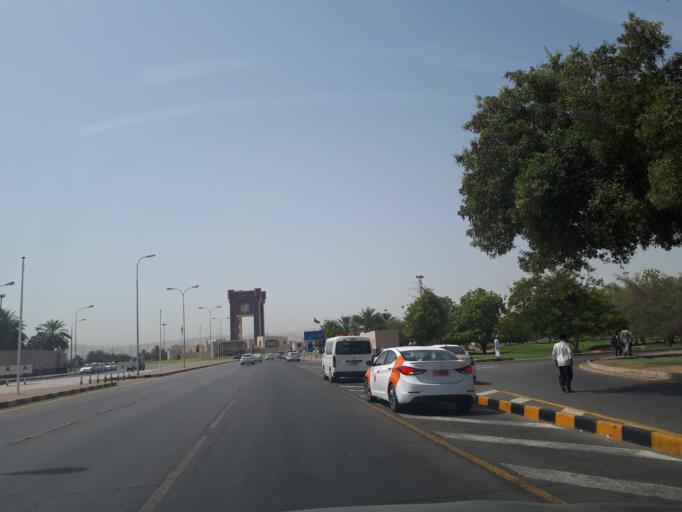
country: OM
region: Muhafazat Masqat
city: As Sib al Jadidah
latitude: 23.5895
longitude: 58.2515
